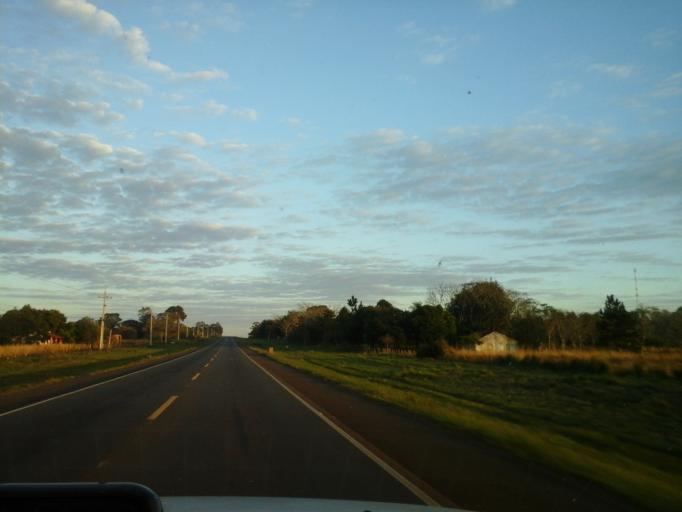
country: PY
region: Misiones
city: San Patricio
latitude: -27.0332
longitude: -56.6806
